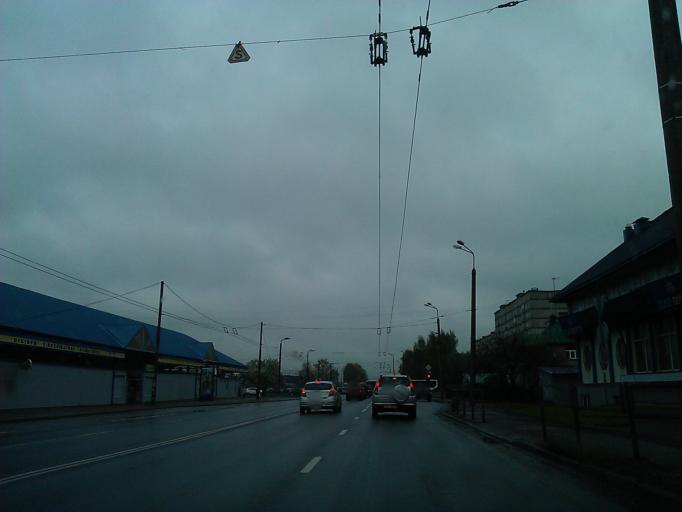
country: LV
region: Riga
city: Riga
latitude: 56.9481
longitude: 24.1941
